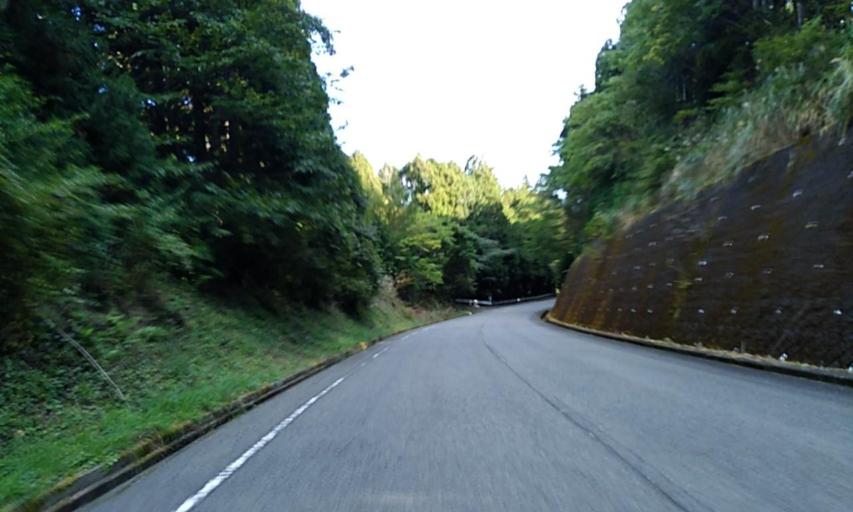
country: JP
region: Wakayama
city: Kainan
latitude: 34.1097
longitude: 135.3319
